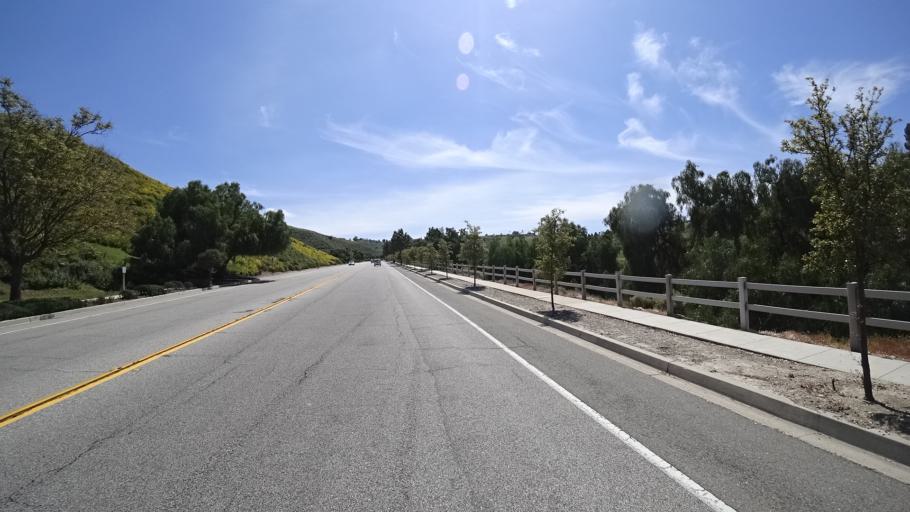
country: US
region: California
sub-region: Ventura County
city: Thousand Oaks
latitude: 34.2339
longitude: -118.8413
